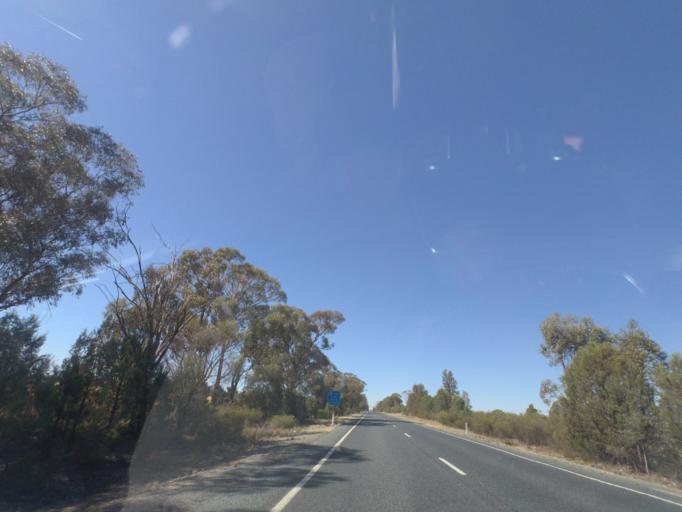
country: AU
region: New South Wales
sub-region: Bland
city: West Wyalong
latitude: -34.1563
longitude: 147.1175
